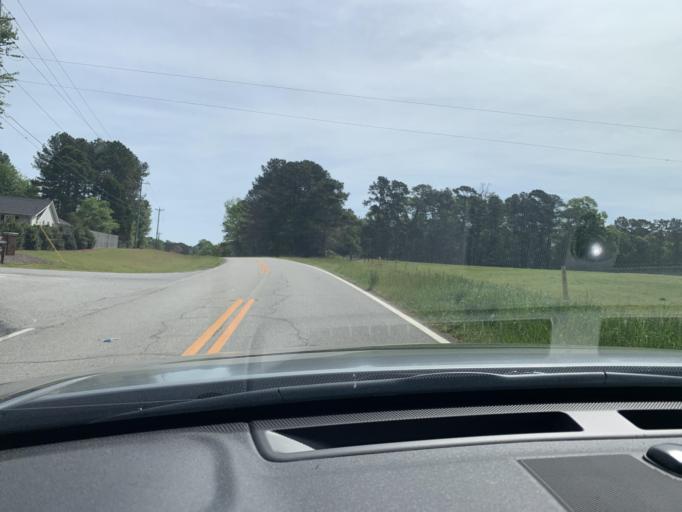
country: US
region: Georgia
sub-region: Oconee County
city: Watkinsville
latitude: 33.8470
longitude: -83.4348
